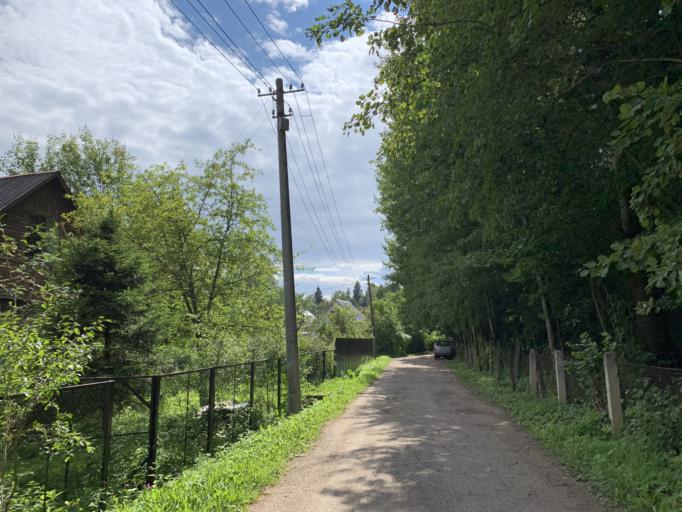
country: RU
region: Moskovskaya
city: Podosinki
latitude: 56.1791
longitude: 37.5755
